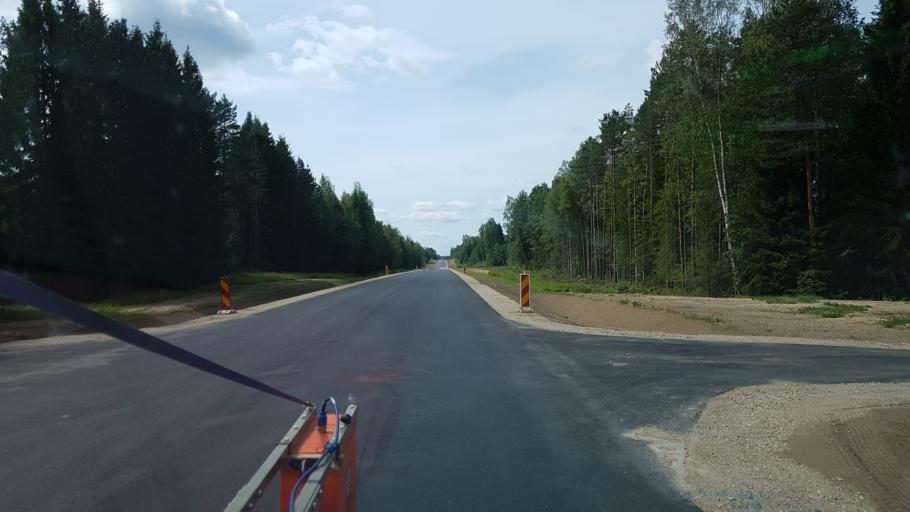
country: RU
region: Pskov
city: Pechory
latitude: 57.6350
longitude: 27.3357
